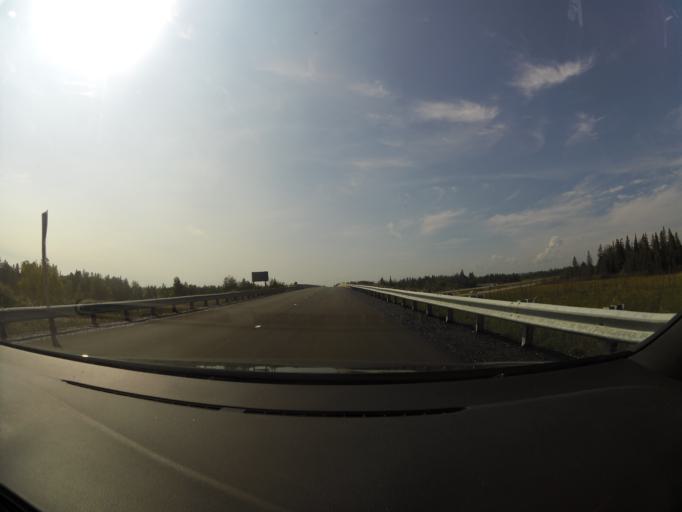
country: CA
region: Ontario
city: Carleton Place
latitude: 45.3337
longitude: -76.1603
